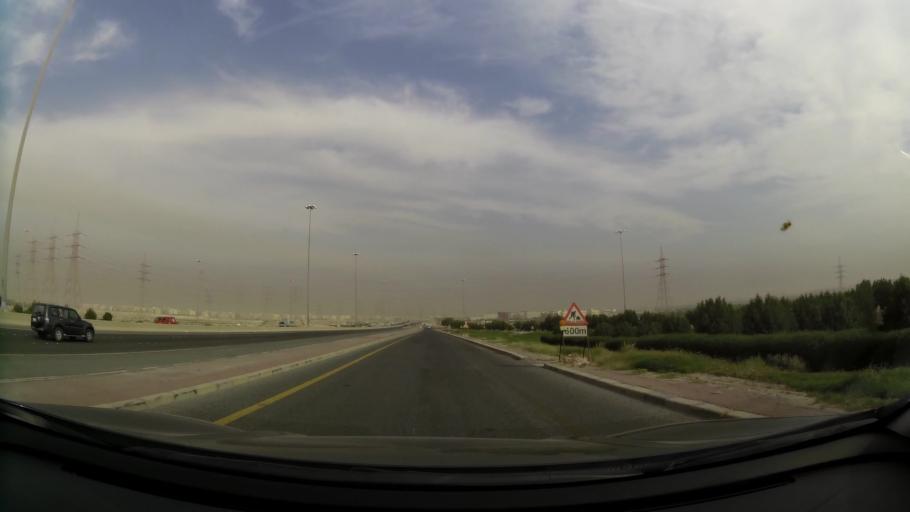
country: KW
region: Muhafazat al Jahra'
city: Al Jahra'
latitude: 29.3139
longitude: 47.7853
